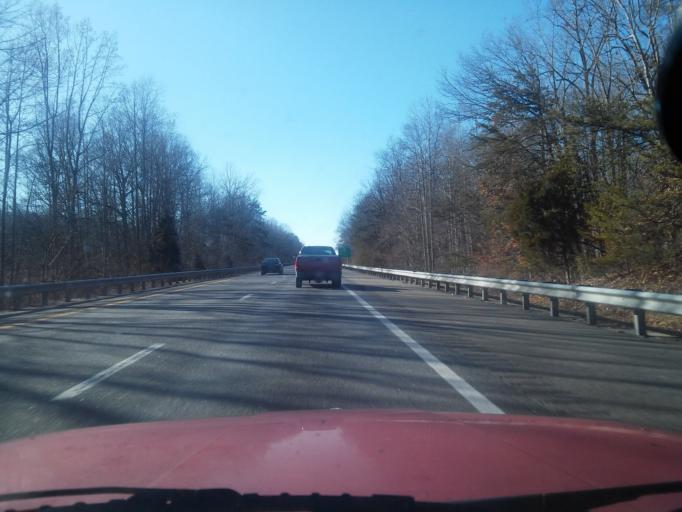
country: US
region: Virginia
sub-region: Fluvanna County
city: Lake Monticello
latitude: 37.9972
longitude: -78.3295
